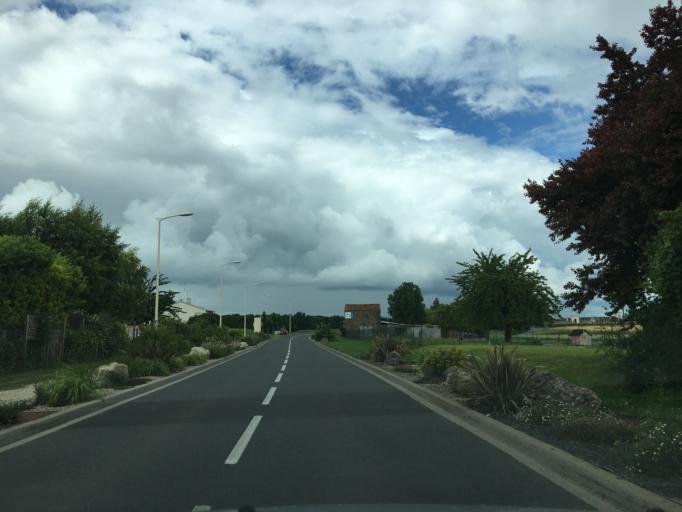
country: FR
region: Poitou-Charentes
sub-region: Departement de la Charente-Maritime
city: Saint-Jean-d'Angely
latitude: 46.0498
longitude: -0.5109
